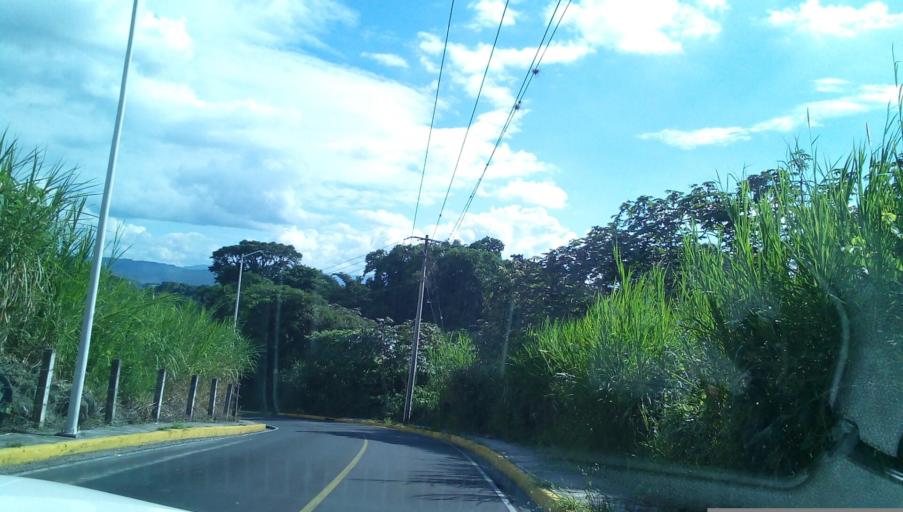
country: MX
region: Veracruz
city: Cordoba
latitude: 18.8957
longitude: -96.9207
